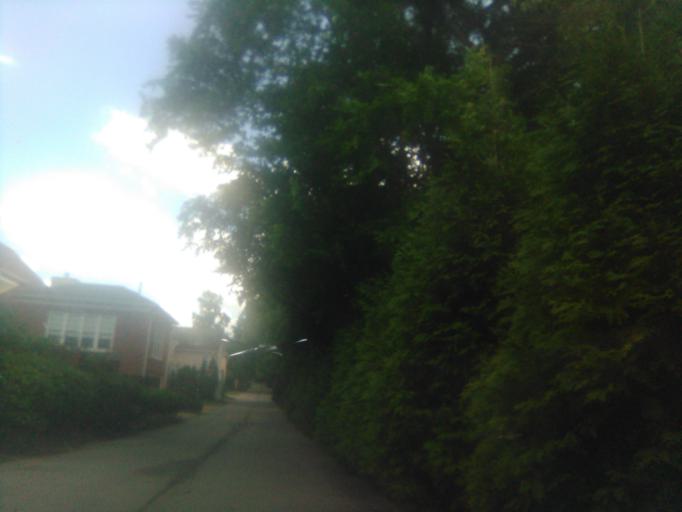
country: US
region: Tennessee
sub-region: Davidson County
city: Belle Meade
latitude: 36.1056
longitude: -86.8297
